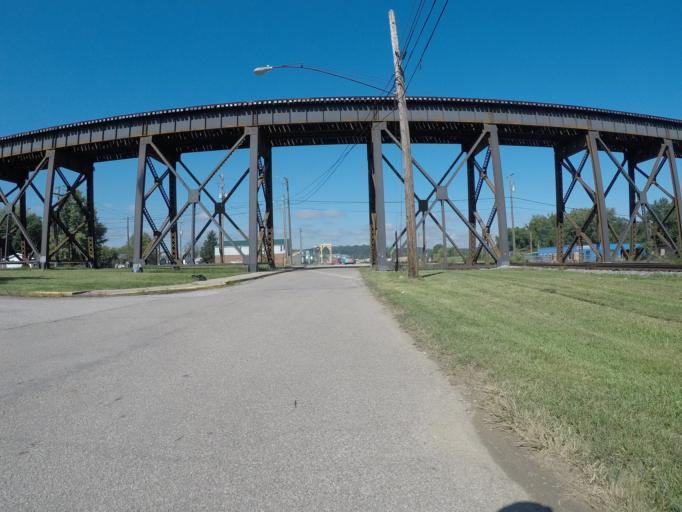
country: US
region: West Virginia
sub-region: Wayne County
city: Kenova
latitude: 38.4023
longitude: -82.5744
